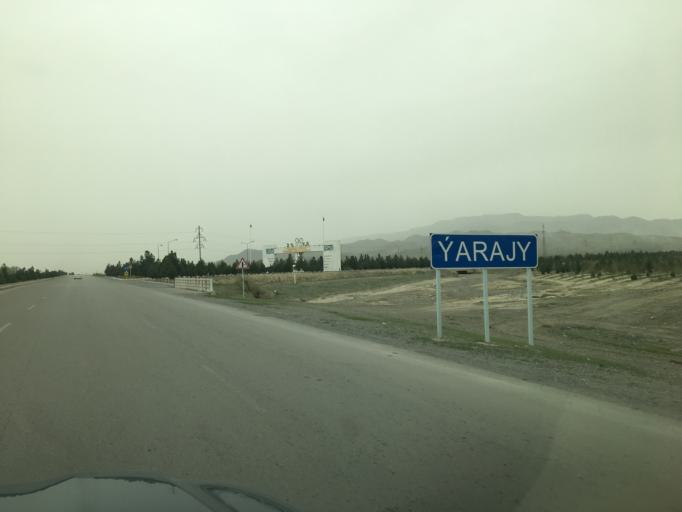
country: TM
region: Ahal
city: Baharly
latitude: 38.2842
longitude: 57.6625
